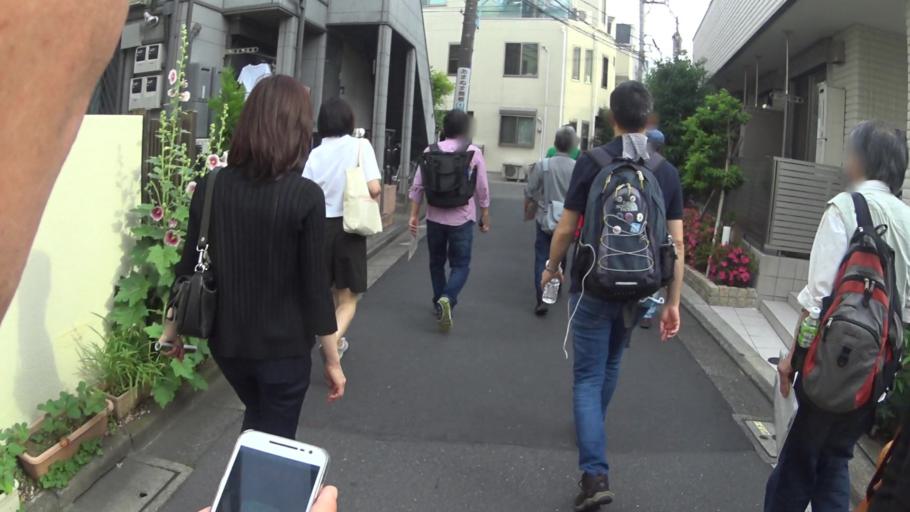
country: JP
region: Tokyo
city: Musashino
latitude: 35.7058
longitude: 139.6253
